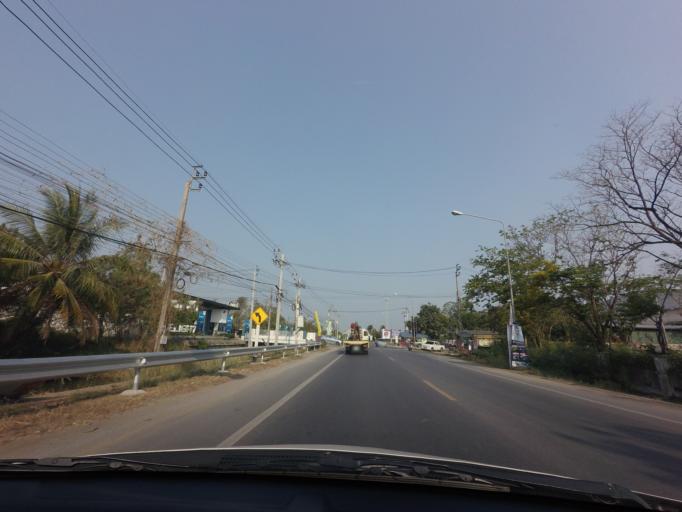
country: TH
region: Nakhon Pathom
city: Salaya
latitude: 13.8117
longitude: 100.3359
